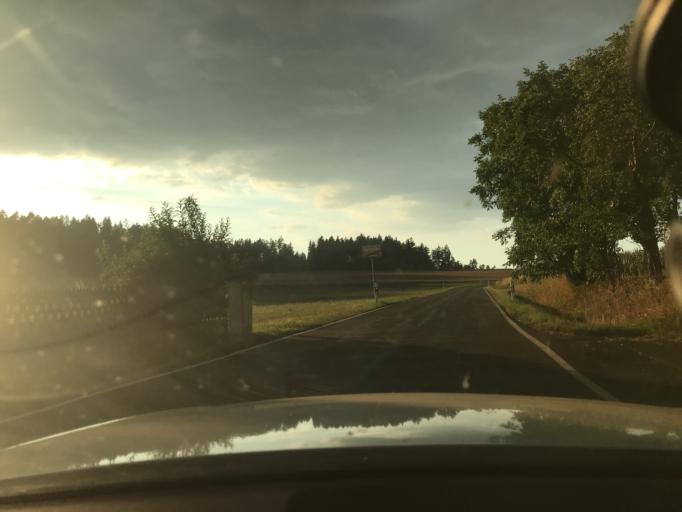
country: DE
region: Bavaria
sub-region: Upper Franconia
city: Pegnitz
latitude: 49.7473
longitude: 11.5880
